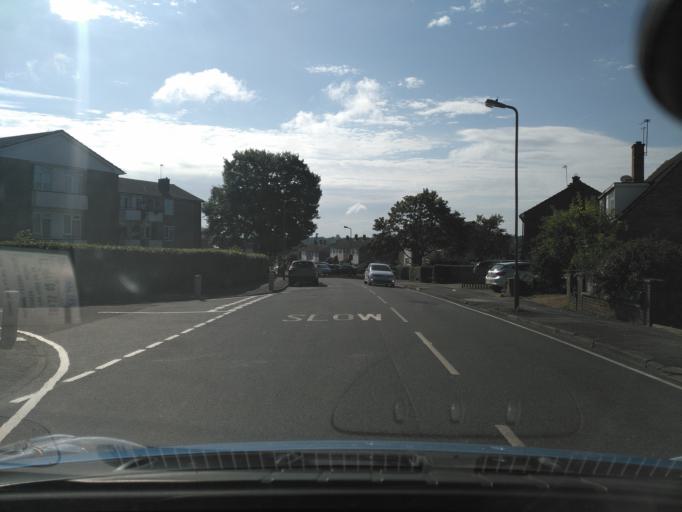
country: GB
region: England
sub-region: Greater London
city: High Barnet
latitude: 51.6471
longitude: -0.2240
